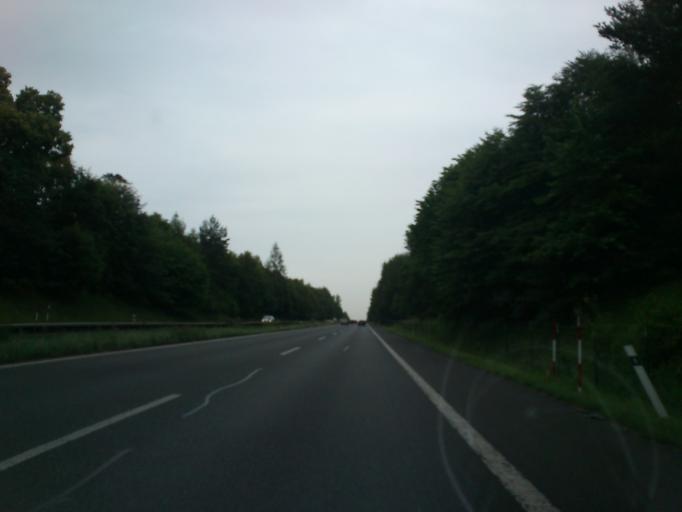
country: CZ
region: Central Bohemia
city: Celakovice
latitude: 50.2321
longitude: 14.7298
